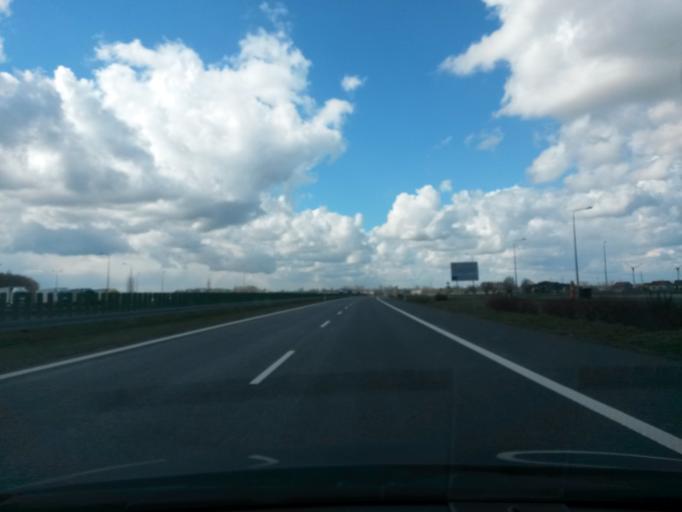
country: PL
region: Lodz Voivodeship
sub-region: Powiat leczycki
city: Swinice Warckie
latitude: 52.0347
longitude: 18.8789
